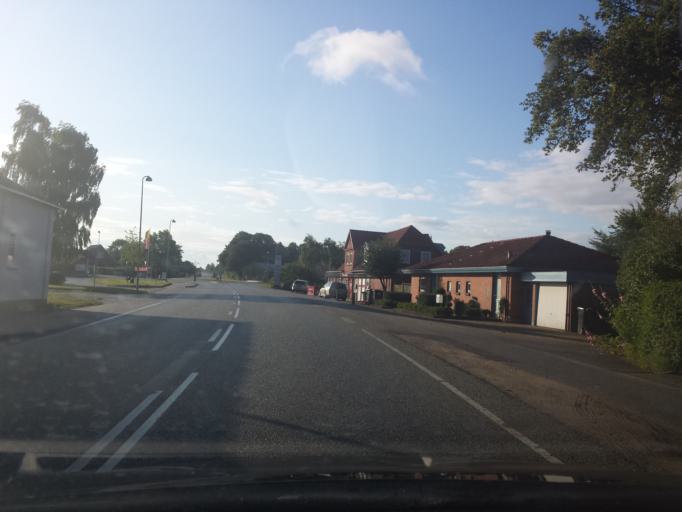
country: DK
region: South Denmark
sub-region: Sonderborg Kommune
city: Broager
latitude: 54.9201
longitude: 9.6805
